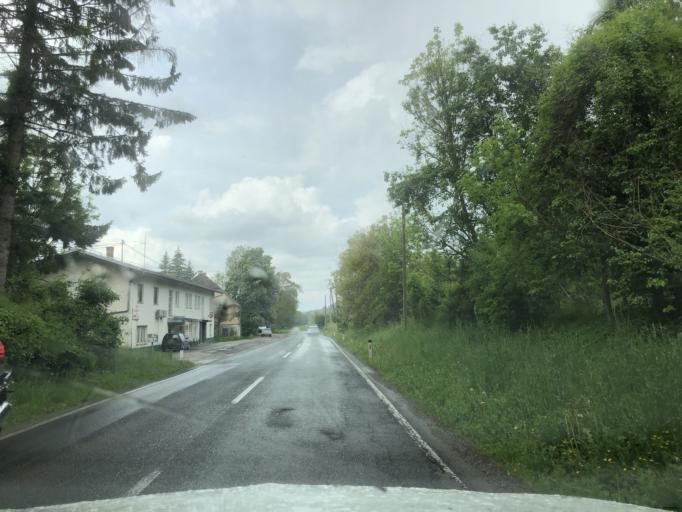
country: SI
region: Cerknica
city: Cerknica
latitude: 45.7807
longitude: 14.3899
